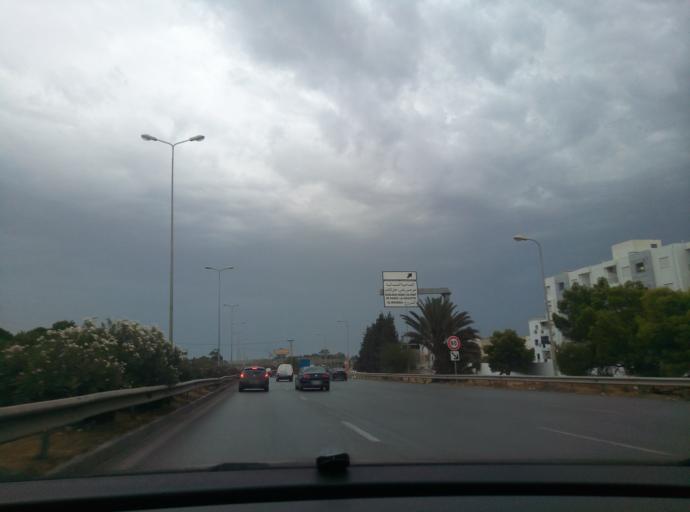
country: TN
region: Bin 'Arus
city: Ben Arous
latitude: 36.7444
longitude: 10.2118
